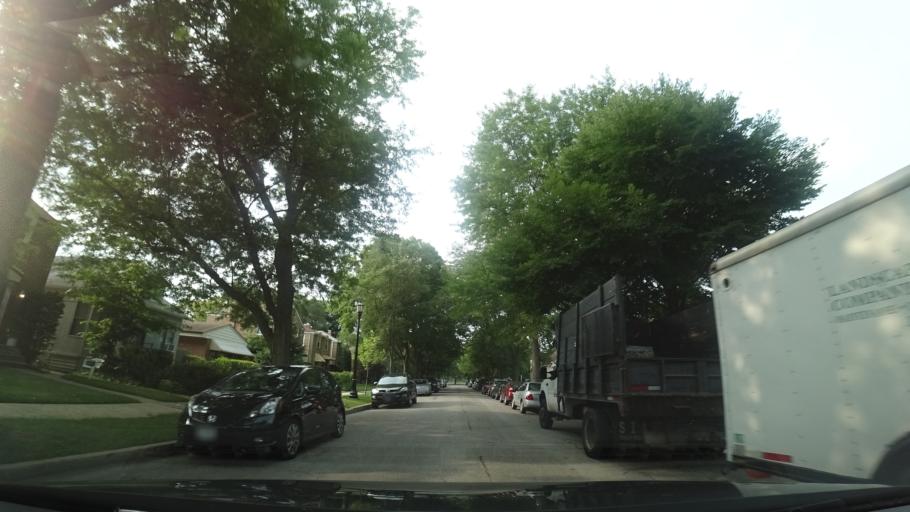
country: US
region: Illinois
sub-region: Cook County
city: Evanston
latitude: 42.0515
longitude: -87.7048
